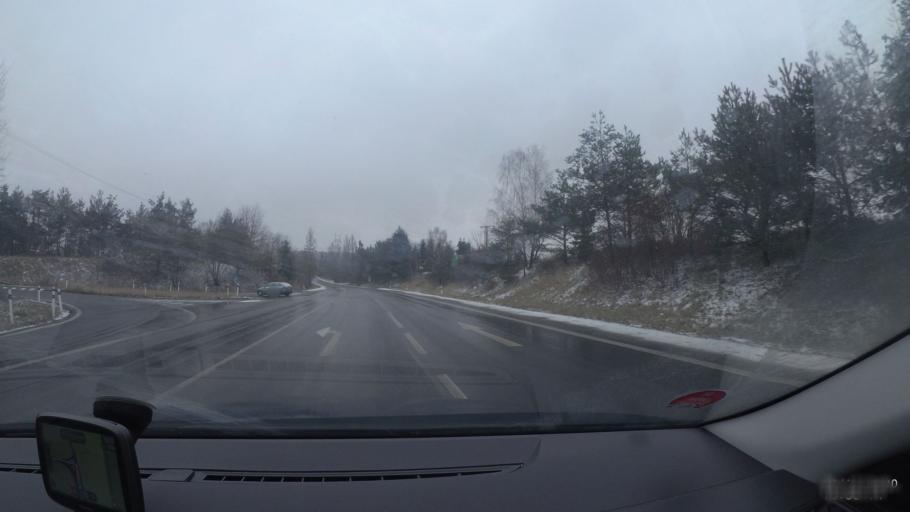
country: CZ
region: Central Bohemia
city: Nove Straseci
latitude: 50.1619
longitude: 13.8980
